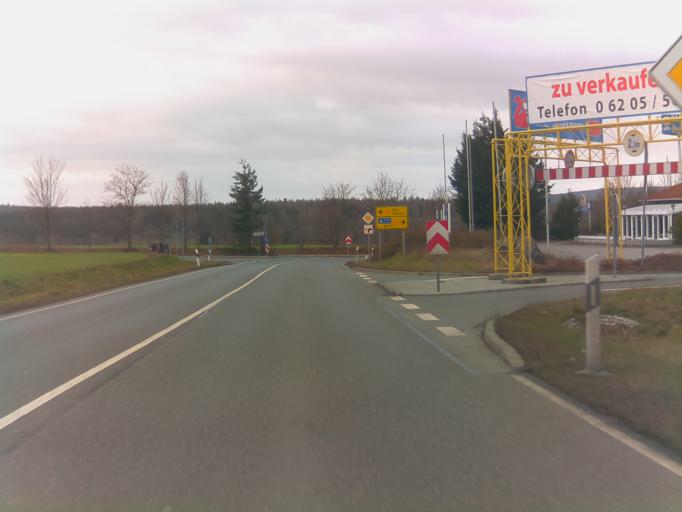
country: DE
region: Thuringia
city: Auma
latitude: 50.6937
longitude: 11.9030
